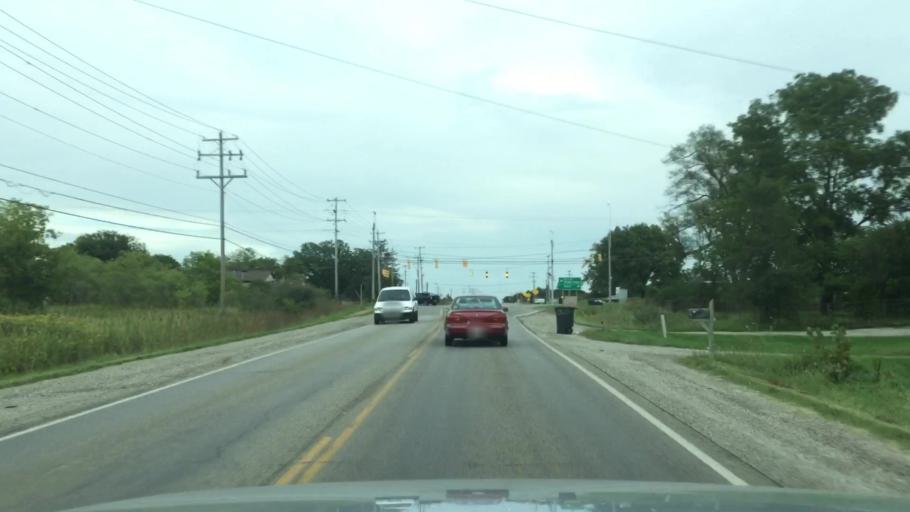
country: US
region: Michigan
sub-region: Genesee County
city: Grand Blanc
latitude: 42.8868
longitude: -83.6323
